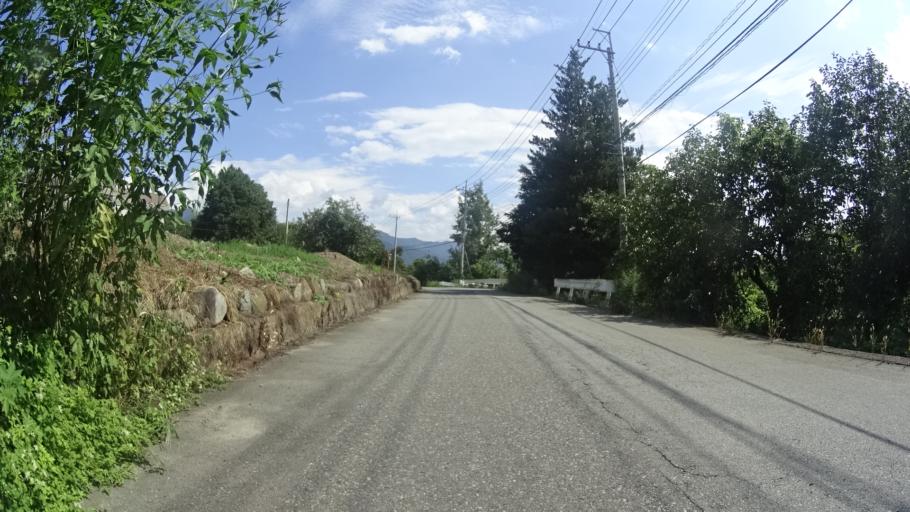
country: JP
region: Yamanashi
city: Enzan
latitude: 35.7270
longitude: 138.7254
